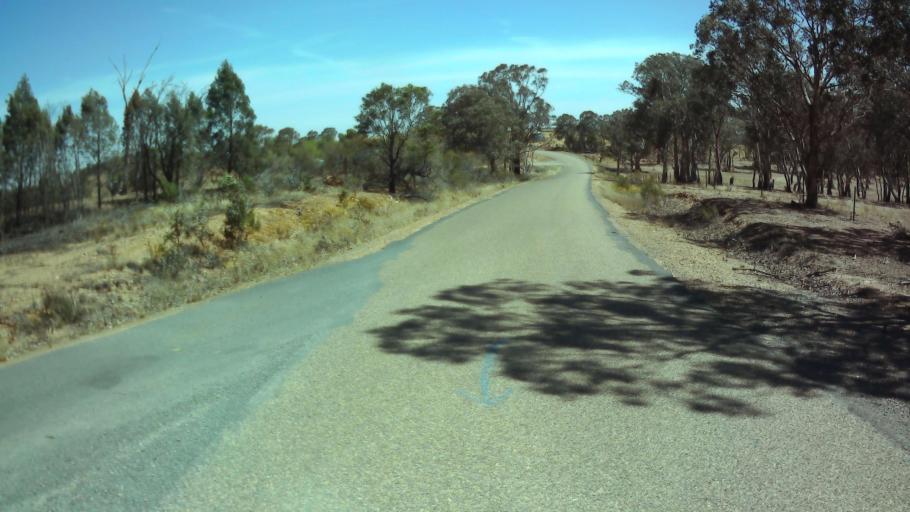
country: AU
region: New South Wales
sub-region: Weddin
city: Grenfell
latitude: -33.9078
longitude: 148.1790
